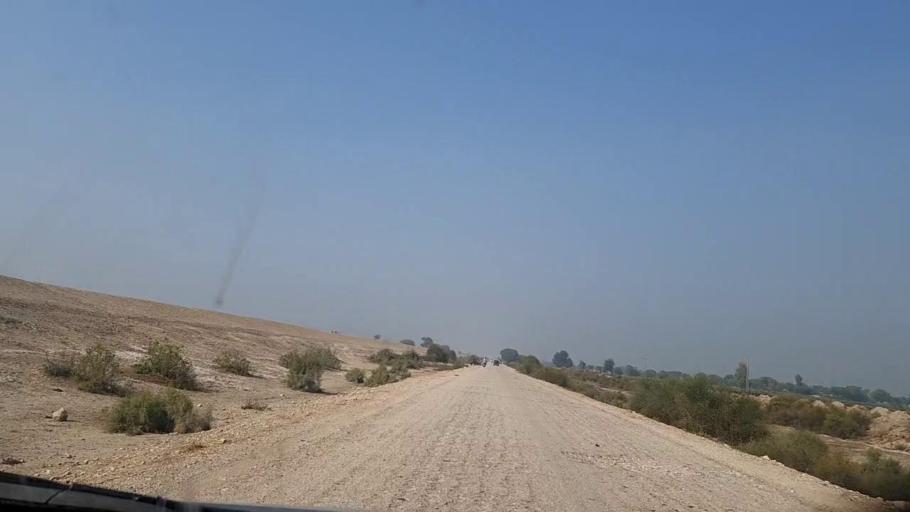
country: PK
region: Sindh
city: Moro
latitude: 26.7118
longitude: 67.9247
